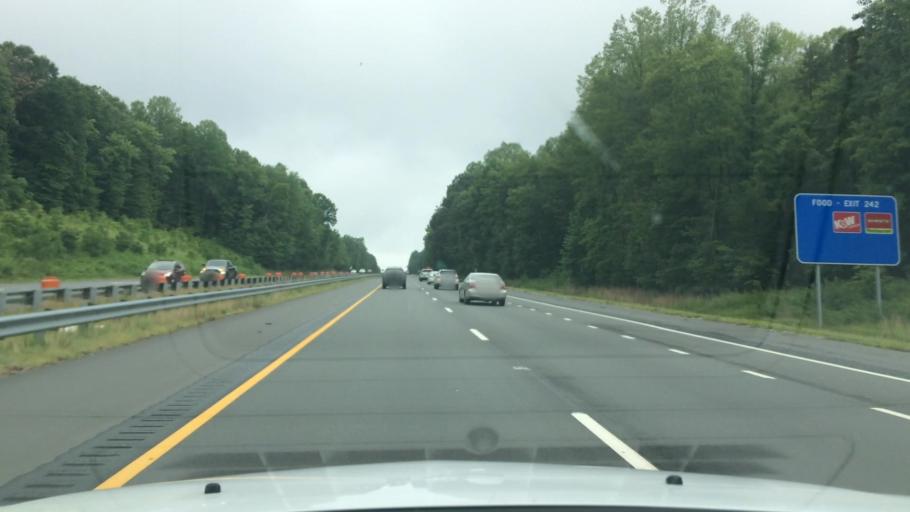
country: US
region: North Carolina
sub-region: Forsyth County
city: Clemmons
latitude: 36.0743
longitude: -80.3691
